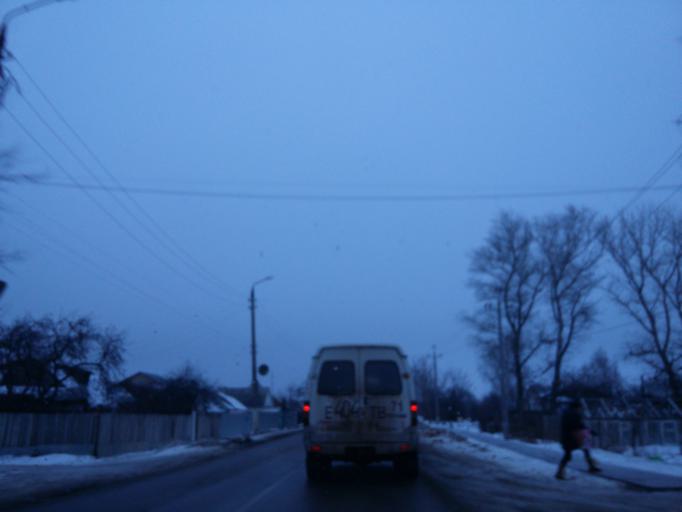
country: RU
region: Tula
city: Shchekino
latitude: 54.0095
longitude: 37.4975
